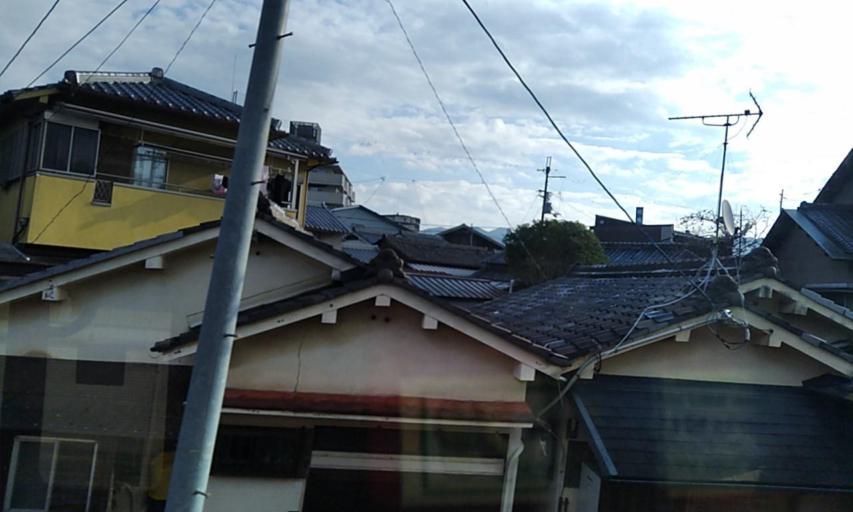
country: JP
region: Nara
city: Kashihara-shi
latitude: 34.4795
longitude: 135.7944
